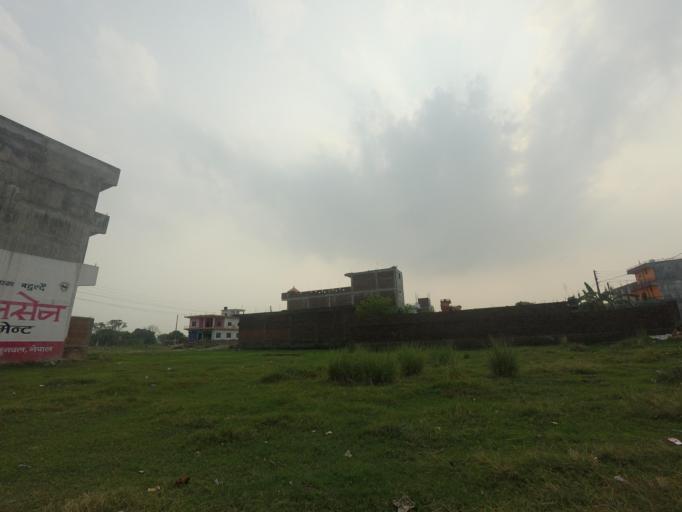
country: NP
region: Western Region
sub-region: Lumbini Zone
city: Bhairahawa
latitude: 27.5106
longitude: 83.4310
